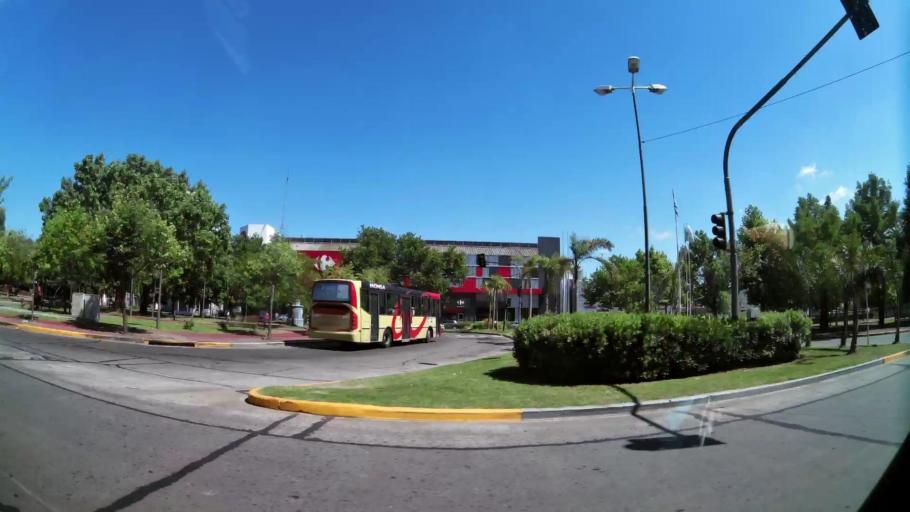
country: AR
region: Buenos Aires
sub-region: Partido de Tigre
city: Tigre
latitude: -34.4340
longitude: -58.5649
